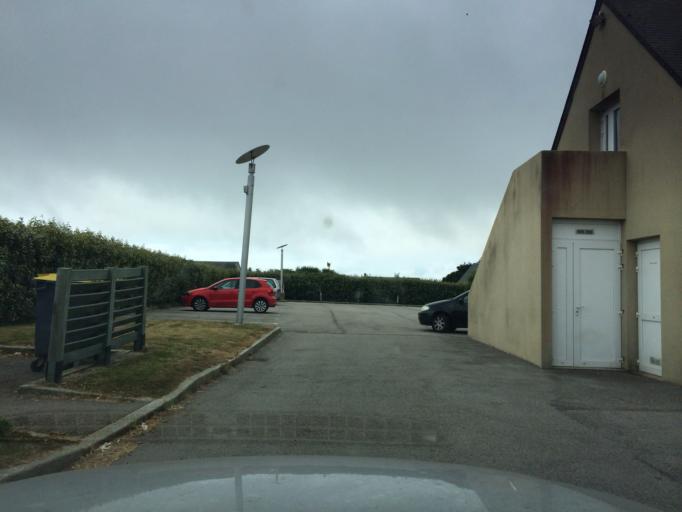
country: FR
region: Lower Normandy
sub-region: Departement de la Manche
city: Beaumont-Hague
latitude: 49.6826
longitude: -1.9034
